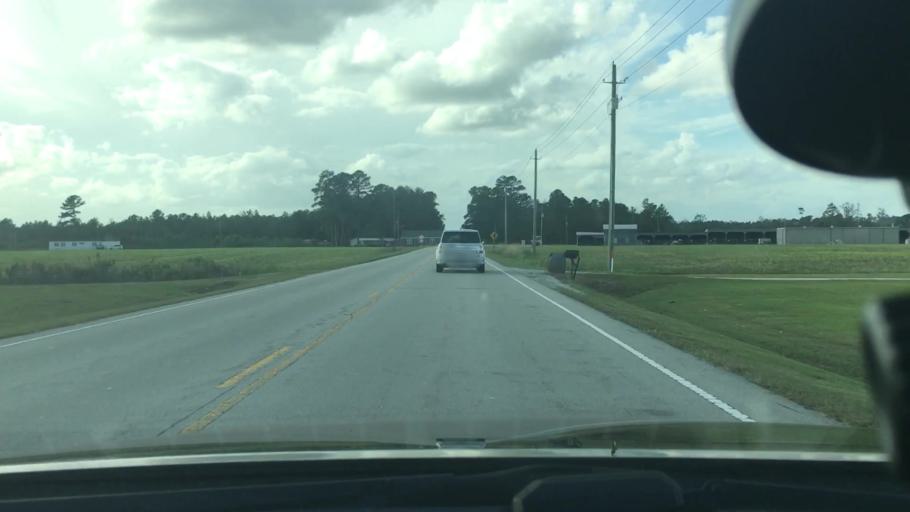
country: US
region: North Carolina
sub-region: Pitt County
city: Windsor
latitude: 35.4735
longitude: -77.2911
